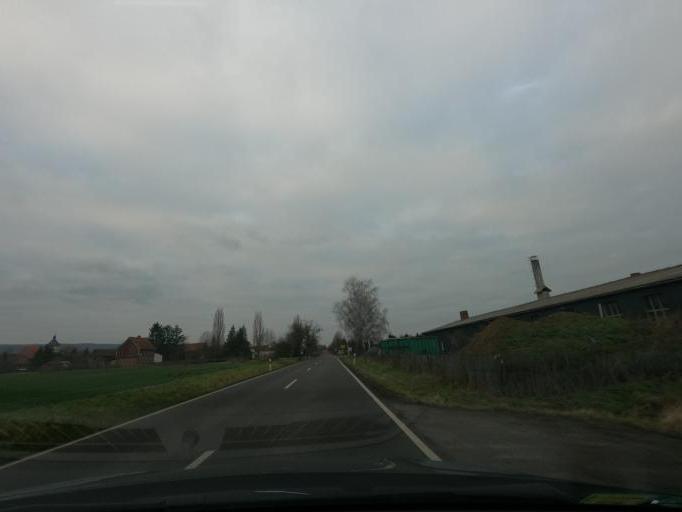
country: DE
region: Lower Saxony
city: Roklum
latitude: 52.0385
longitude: 10.7505
